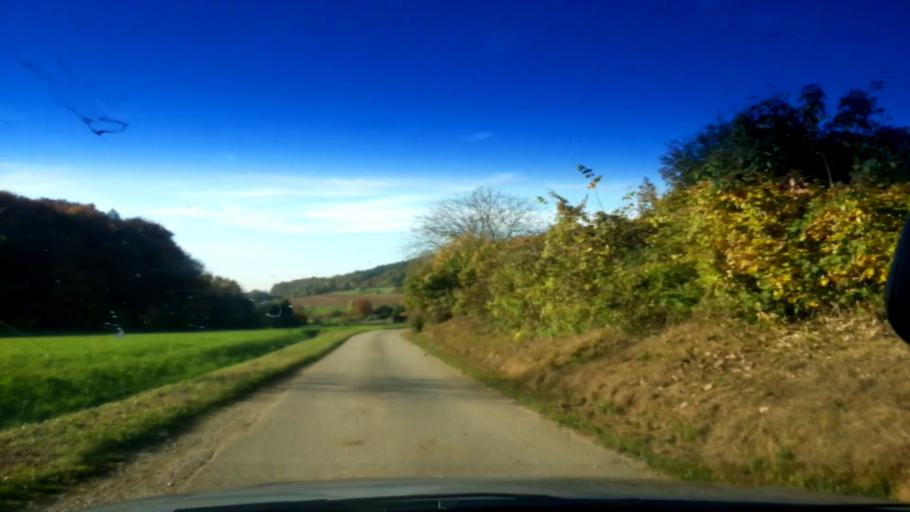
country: DE
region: Bavaria
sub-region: Upper Franconia
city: Litzendorf
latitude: 49.8978
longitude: 11.0456
